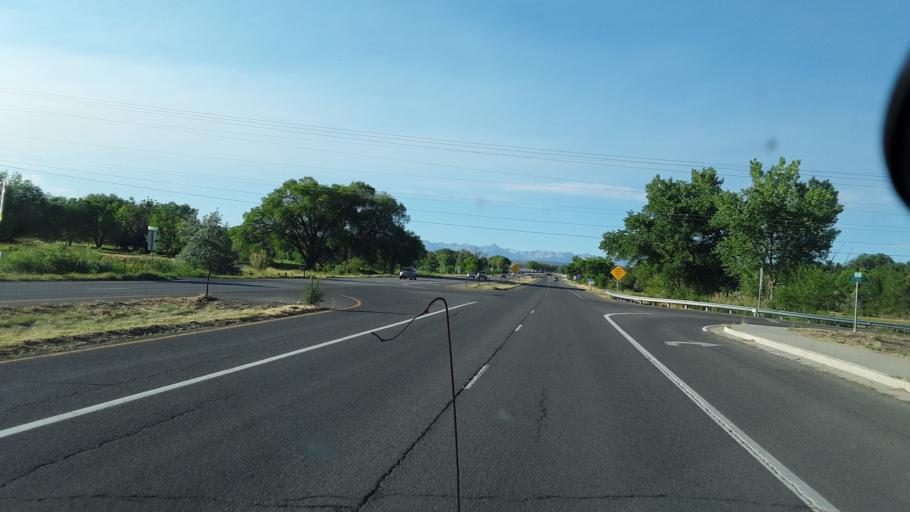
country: US
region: Colorado
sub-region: Montrose County
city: Montrose
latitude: 38.4407
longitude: -107.8669
